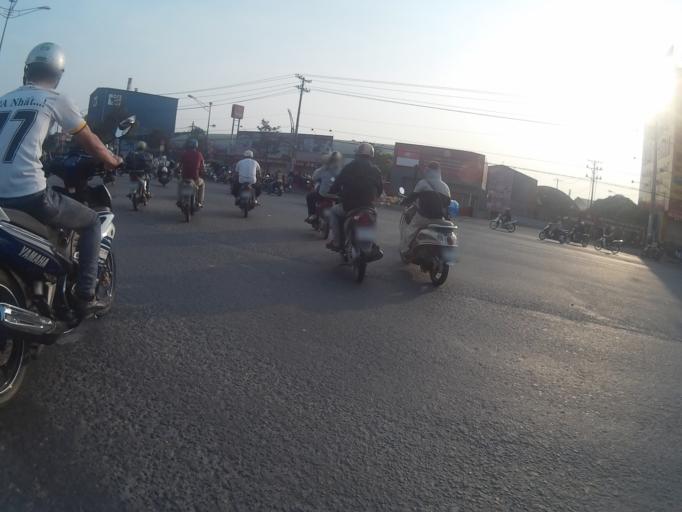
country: VN
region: Ho Chi Minh City
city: Ho Chi Minh City
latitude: 10.8232
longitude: 106.6297
